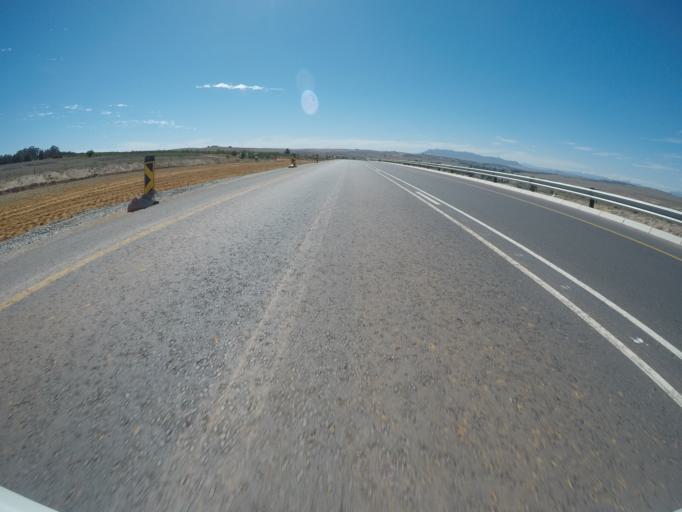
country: ZA
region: Western Cape
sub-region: West Coast District Municipality
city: Malmesbury
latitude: -33.4995
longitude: 18.6647
